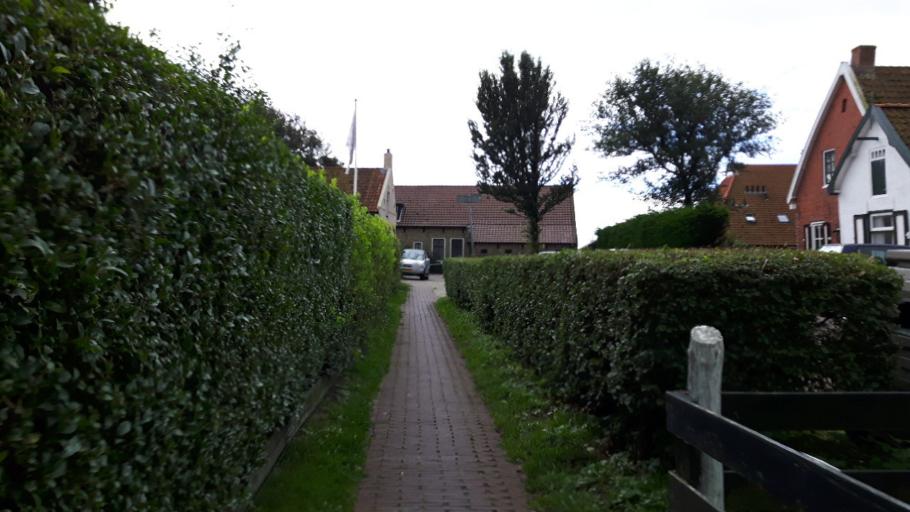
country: NL
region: Friesland
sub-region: Gemeente Ameland
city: Hollum
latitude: 53.4396
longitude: 5.6378
